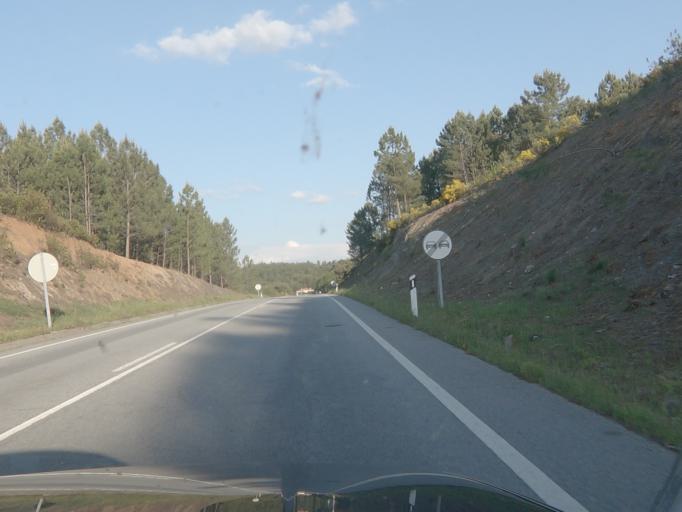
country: PT
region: Portalegre
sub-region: Marvao
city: Marvao
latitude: 39.3712
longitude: -7.3490
